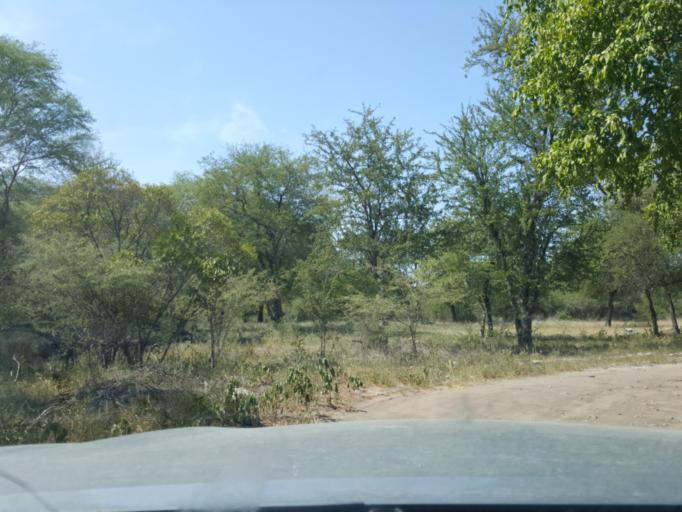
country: BW
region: North West
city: Shakawe
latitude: -18.7595
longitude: 21.7378
